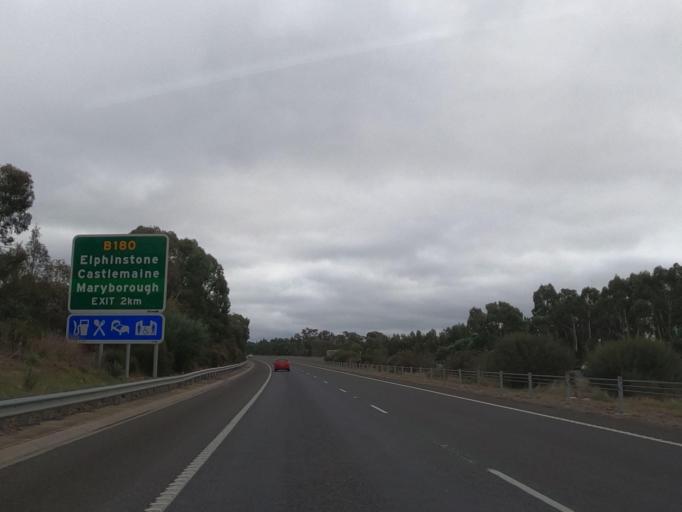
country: AU
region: Victoria
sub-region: Mount Alexander
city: Castlemaine
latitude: -37.0960
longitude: 144.3564
